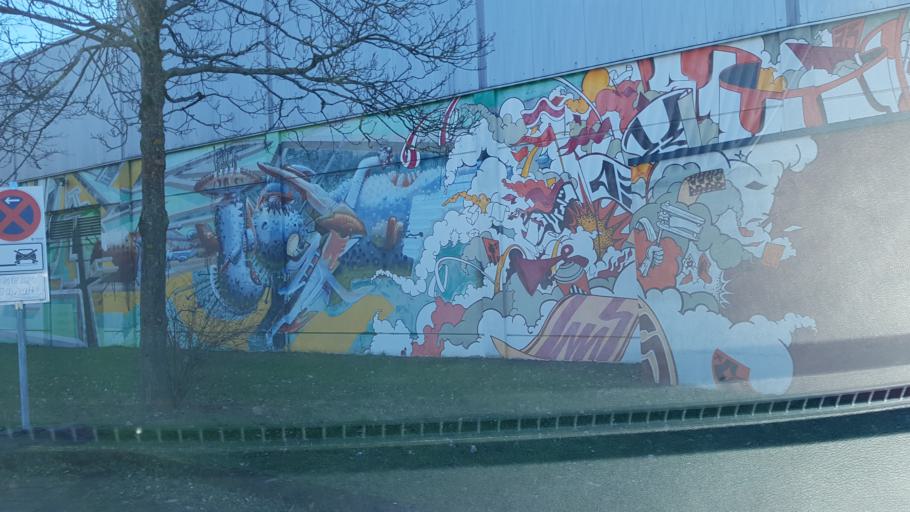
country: DE
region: North Rhine-Westphalia
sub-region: Regierungsbezirk Koln
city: Hennef
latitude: 50.7779
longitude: 7.2675
